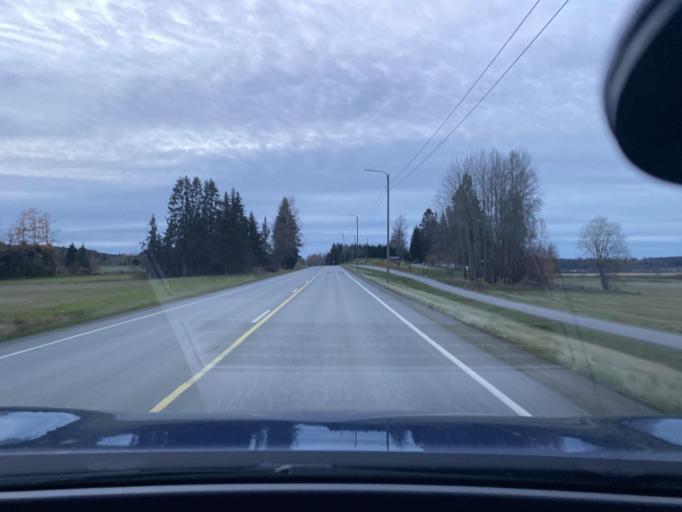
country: FI
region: Uusimaa
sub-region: Helsinki
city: Saukkola
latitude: 60.3846
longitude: 23.9303
